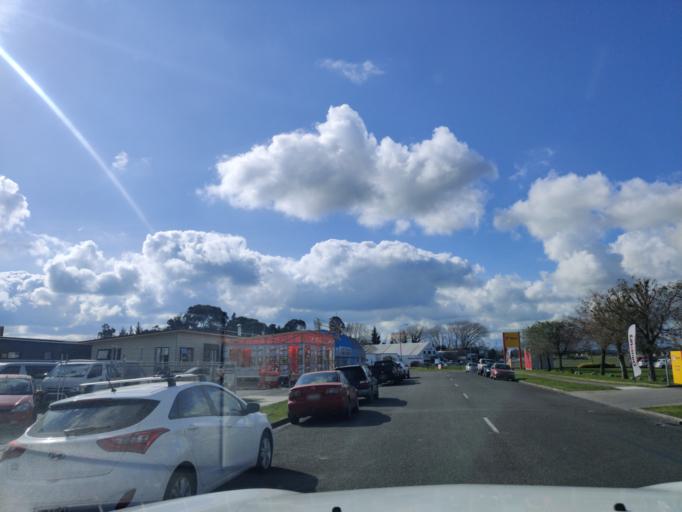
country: NZ
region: Manawatu-Wanganui
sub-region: Palmerston North City
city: Palmerston North
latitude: -40.3392
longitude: 175.6002
